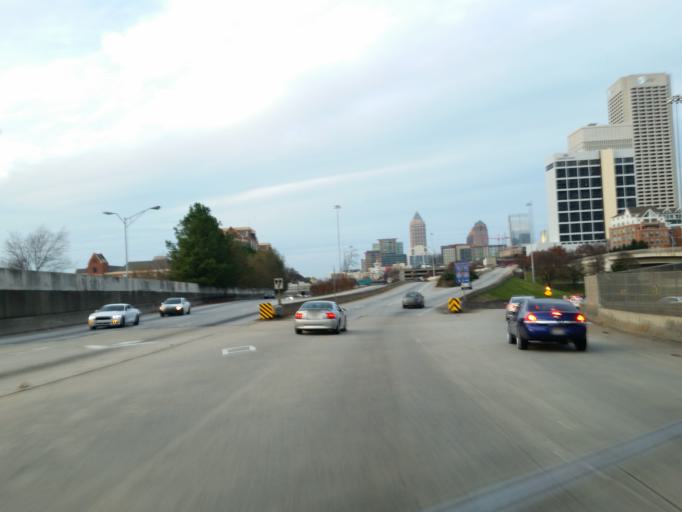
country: US
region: Georgia
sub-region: Fulton County
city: Atlanta
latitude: 33.7653
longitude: -84.3903
